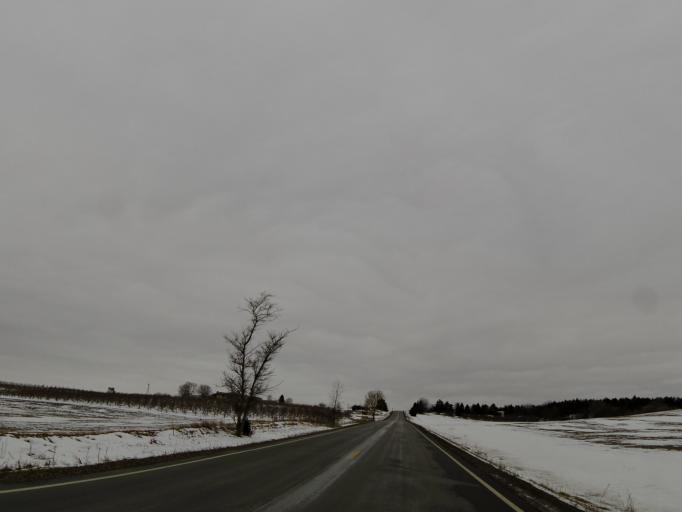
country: US
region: Wisconsin
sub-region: Pierce County
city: Prescott
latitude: 44.7901
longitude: -92.8116
